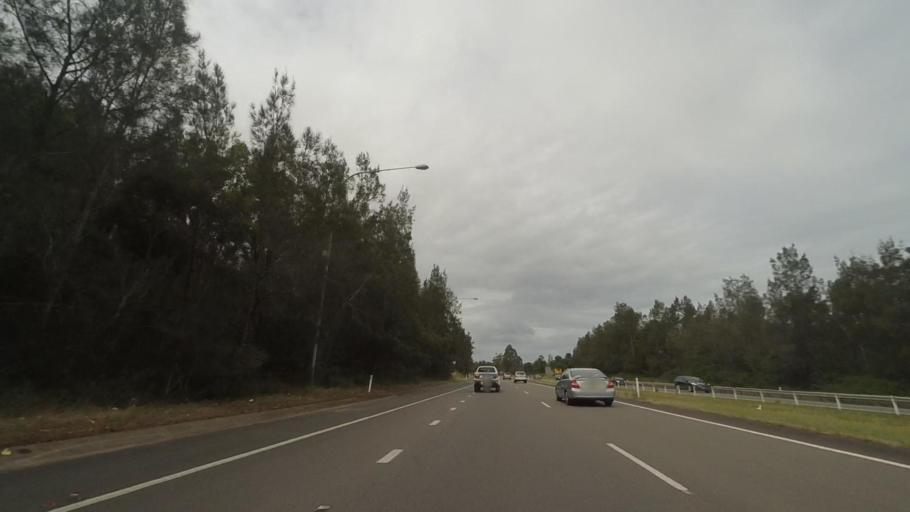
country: AU
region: New South Wales
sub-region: Port Stephens Shire
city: Raymond Terrace
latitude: -32.7448
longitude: 151.7724
